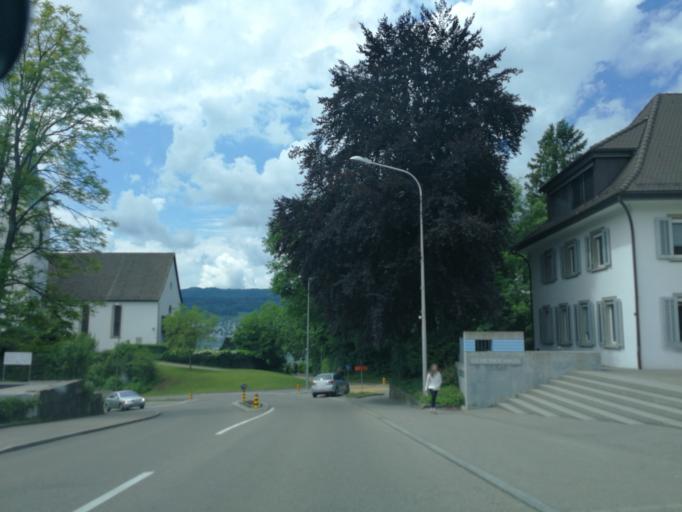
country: CH
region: Zurich
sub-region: Bezirk Meilen
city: Herrliberg
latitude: 47.2852
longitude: 8.6113
